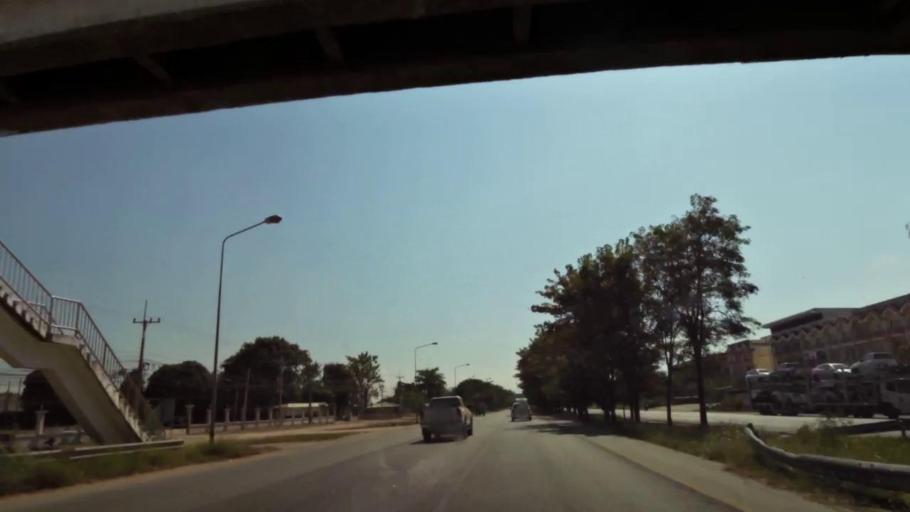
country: TH
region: Nakhon Sawan
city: Kao Liao
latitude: 15.8694
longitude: 100.1166
